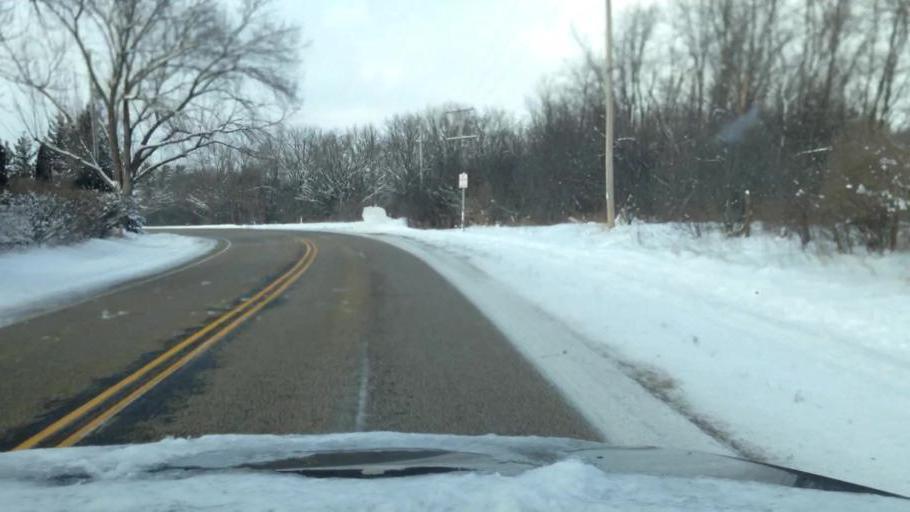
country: US
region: Wisconsin
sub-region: Walworth County
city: East Troy
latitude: 42.8402
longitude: -88.4242
